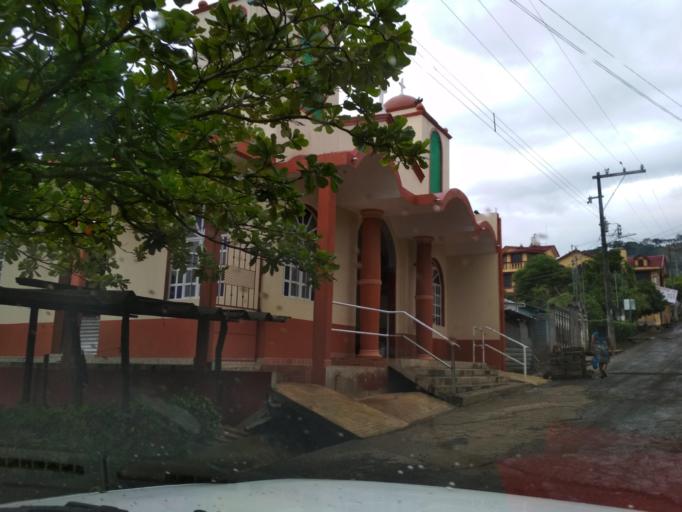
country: MX
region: Veracruz
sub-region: San Andres Tuxtla
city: San Isidro Xoteapan (San Isidro Texcaltitan)
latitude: 18.4623
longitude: -95.2343
